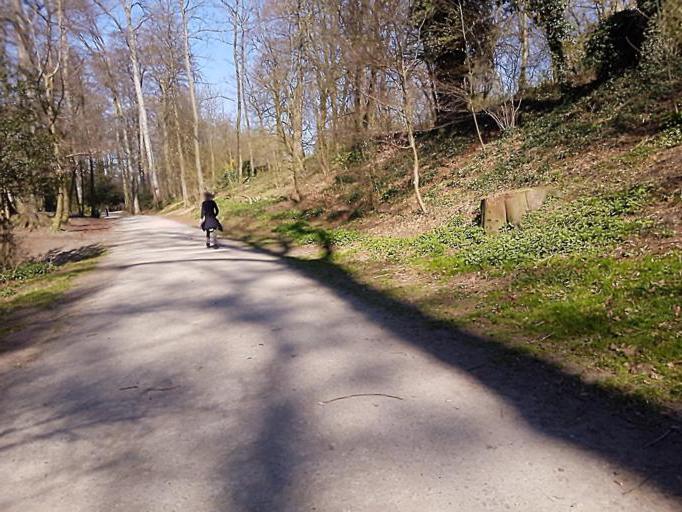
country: BE
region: Flanders
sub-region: Provincie Vlaams-Brabant
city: Drogenbos
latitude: 50.8159
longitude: 4.3332
